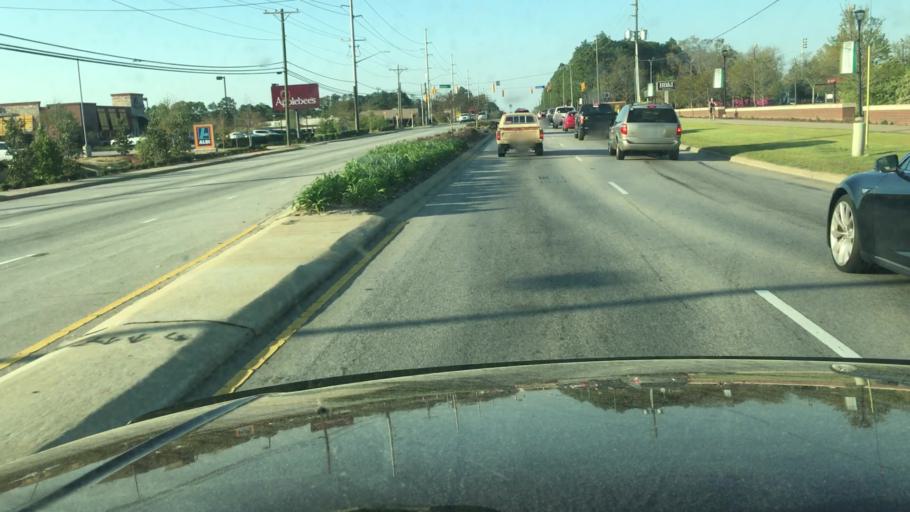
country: US
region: North Carolina
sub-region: Cumberland County
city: Fayetteville
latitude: 35.1305
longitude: -78.8782
